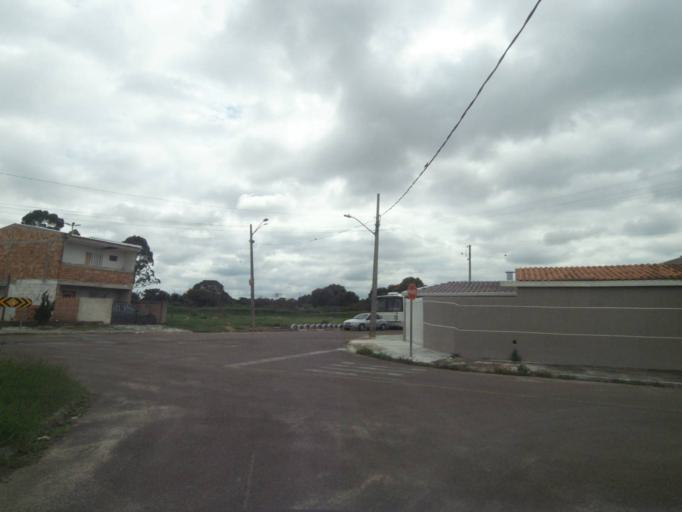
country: BR
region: Parana
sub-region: Pinhais
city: Pinhais
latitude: -25.4459
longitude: -49.2002
